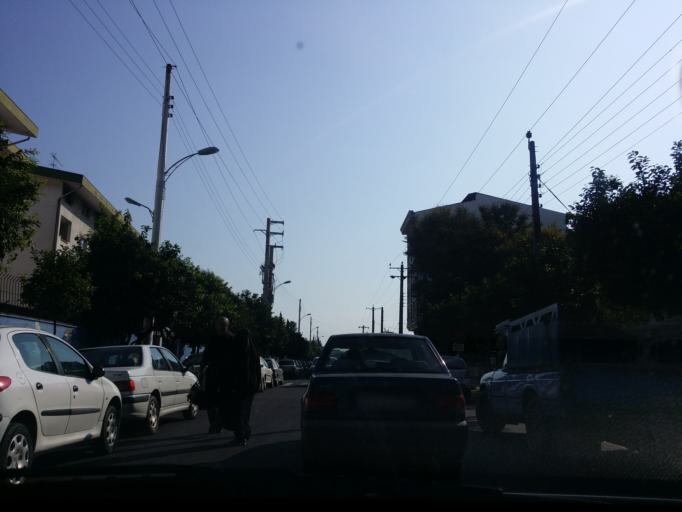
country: IR
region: Mazandaran
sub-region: Nowshahr
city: Nowshahr
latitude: 36.6523
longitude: 51.4973
